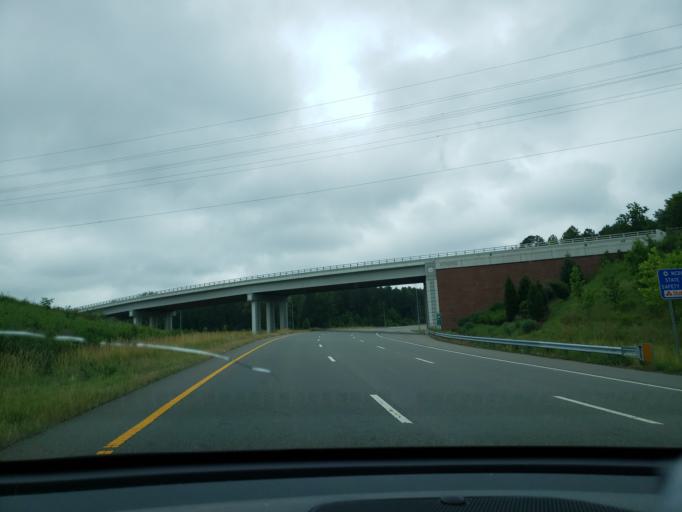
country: US
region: North Carolina
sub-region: Wake County
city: Morrisville
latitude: 35.8578
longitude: -78.8619
